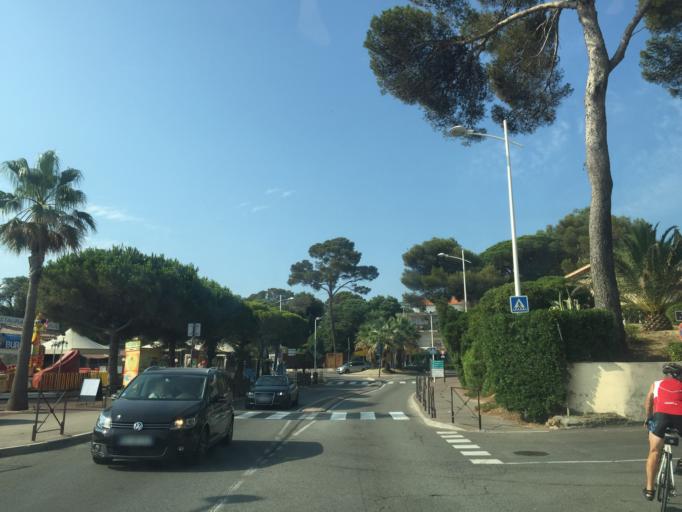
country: FR
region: Provence-Alpes-Cote d'Azur
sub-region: Departement du Var
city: Frejus
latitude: 43.3923
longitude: 6.7281
